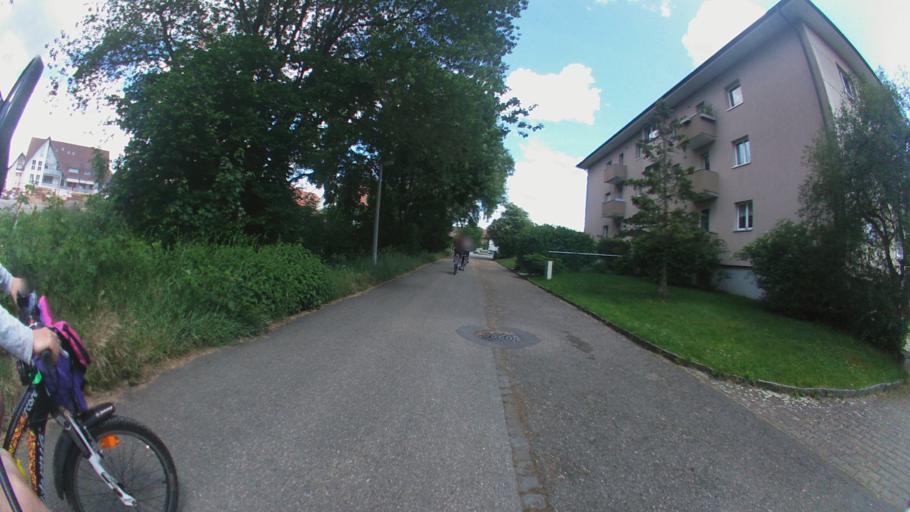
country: CH
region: Zurich
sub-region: Bezirk Dielsdorf
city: Regensdorf
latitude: 47.4426
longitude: 8.4780
